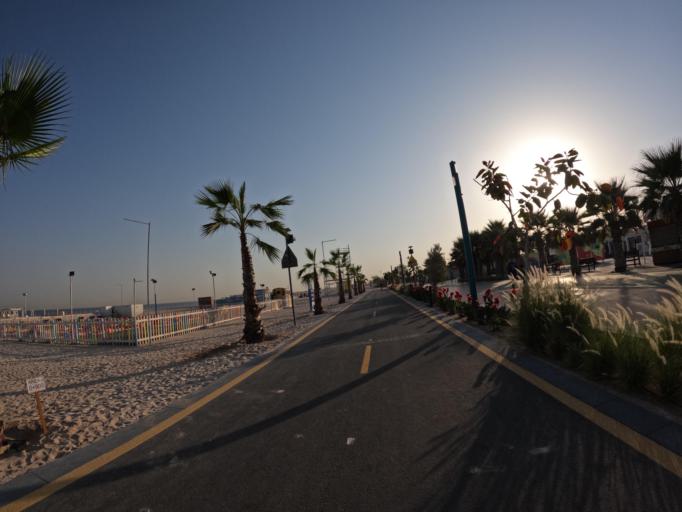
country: AE
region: Dubai
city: Dubai
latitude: 25.1648
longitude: 55.2081
